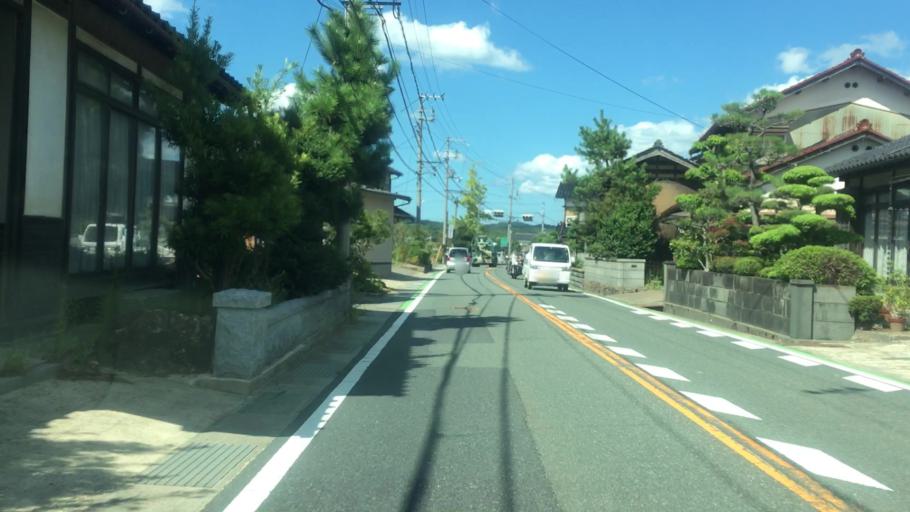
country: JP
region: Kyoto
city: Miyazu
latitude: 35.5888
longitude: 135.0385
